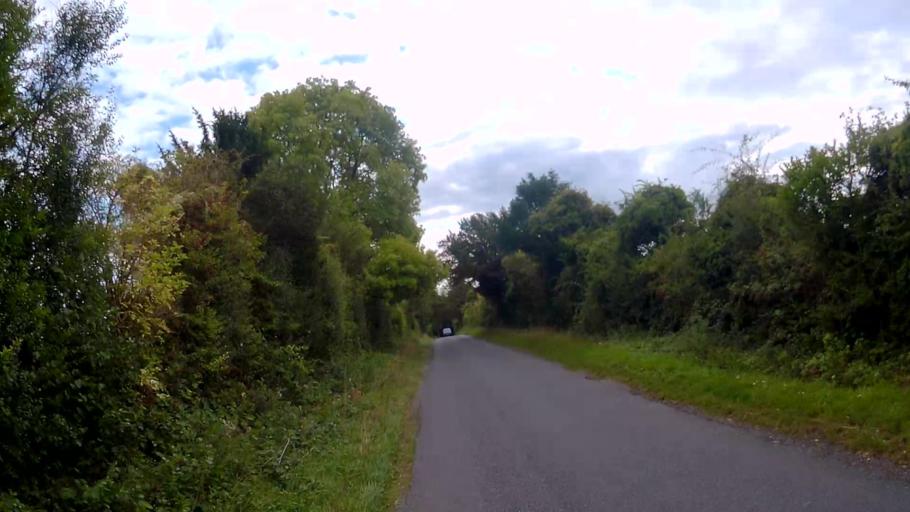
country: GB
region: England
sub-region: Hampshire
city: Kings Worthy
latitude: 51.1578
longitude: -1.3253
